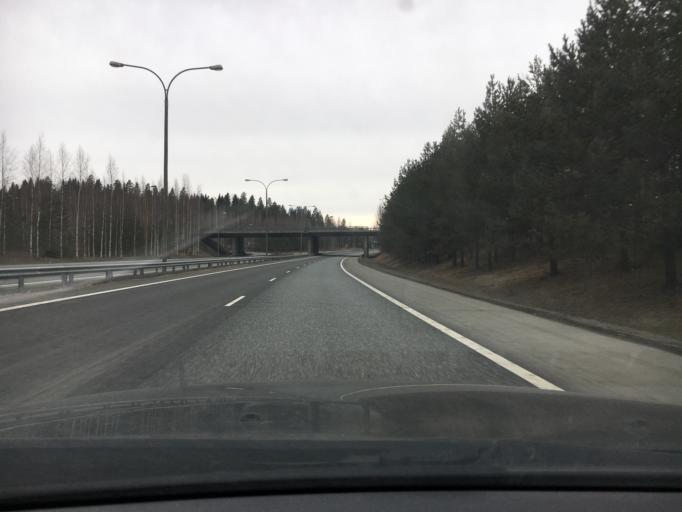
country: FI
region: Northern Savo
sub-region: Kuopio
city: Siilinjaervi
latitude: 63.0723
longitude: 27.6553
